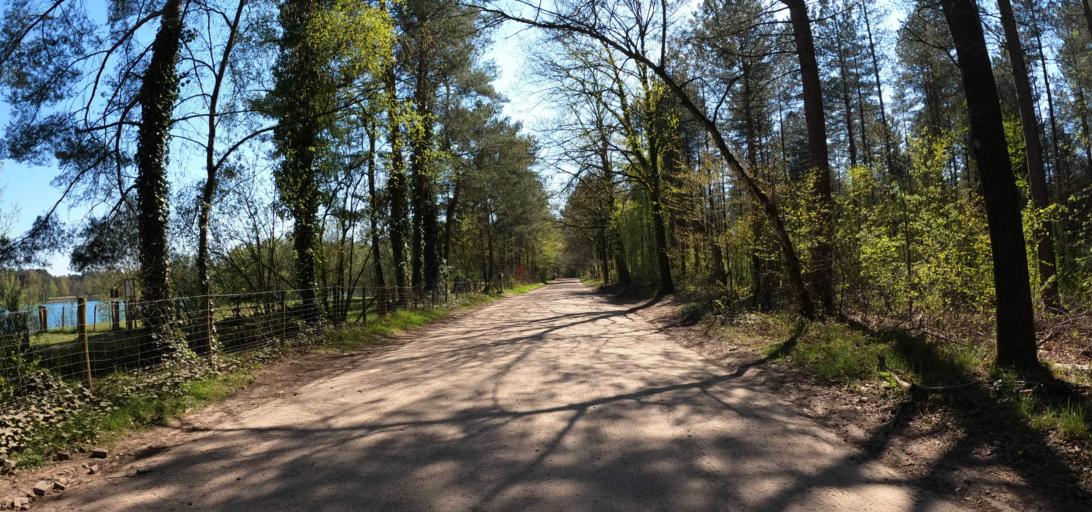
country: BE
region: Flanders
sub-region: Provincie Antwerpen
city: Lille
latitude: 51.2758
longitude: 4.8283
